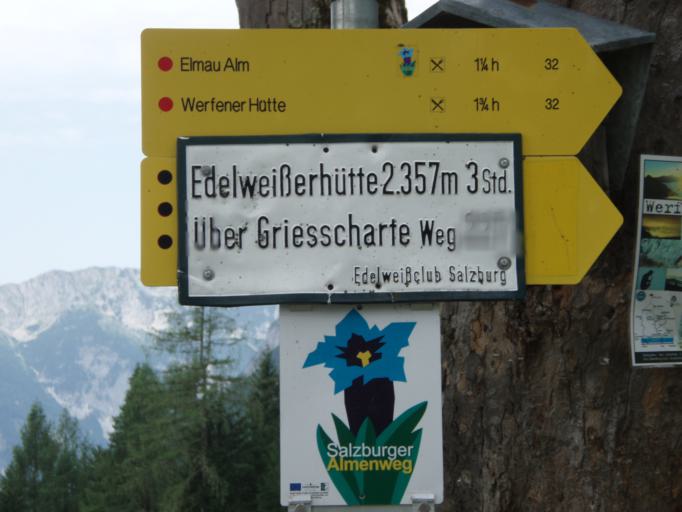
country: AT
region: Salzburg
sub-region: Politischer Bezirk Sankt Johann im Pongau
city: Pfarrwerfen
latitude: 47.4810
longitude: 13.2226
